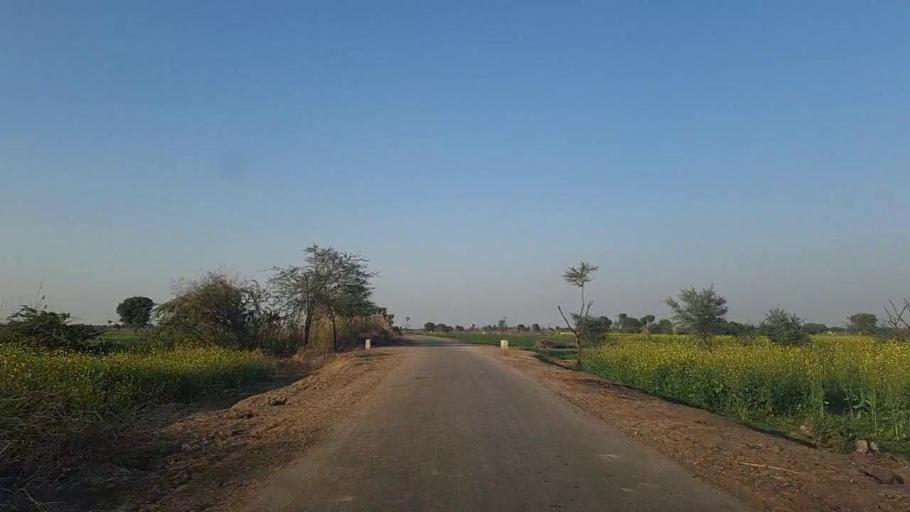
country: PK
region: Sindh
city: Jam Sahib
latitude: 26.3451
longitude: 68.6733
